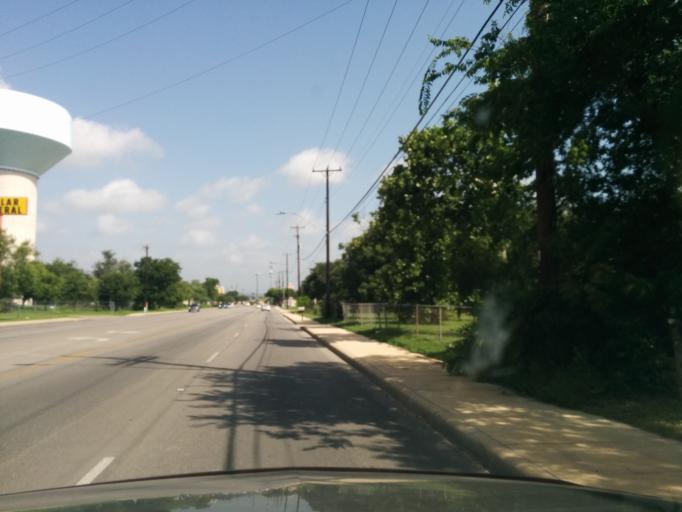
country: US
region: Texas
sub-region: Bexar County
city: Leon Valley
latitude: 29.5413
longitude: -98.6120
